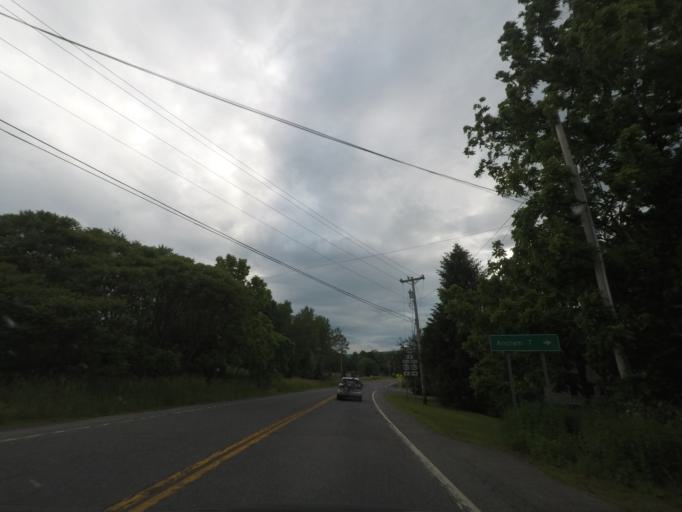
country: US
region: New York
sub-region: Dutchess County
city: Pine Plains
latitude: 41.9733
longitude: -73.6299
